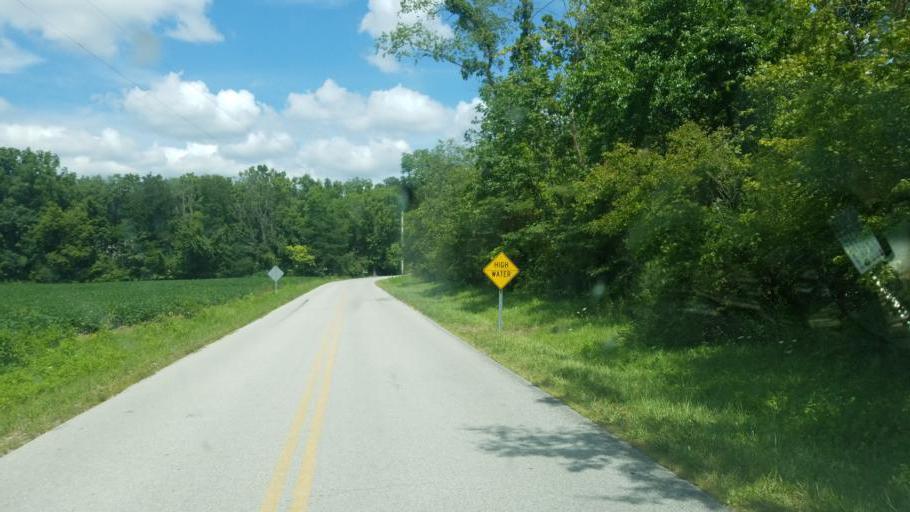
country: US
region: Ohio
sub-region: Delaware County
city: Sunbury
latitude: 40.2956
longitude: -82.8262
